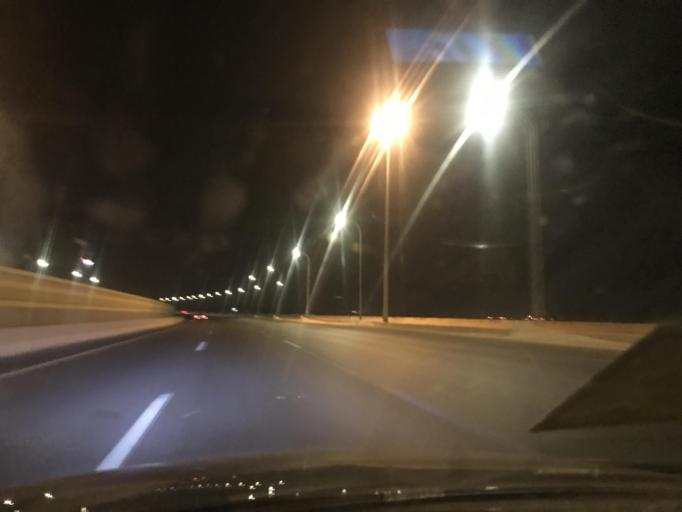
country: SA
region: Ar Riyad
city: Riyadh
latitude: 24.9016
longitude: 46.7042
